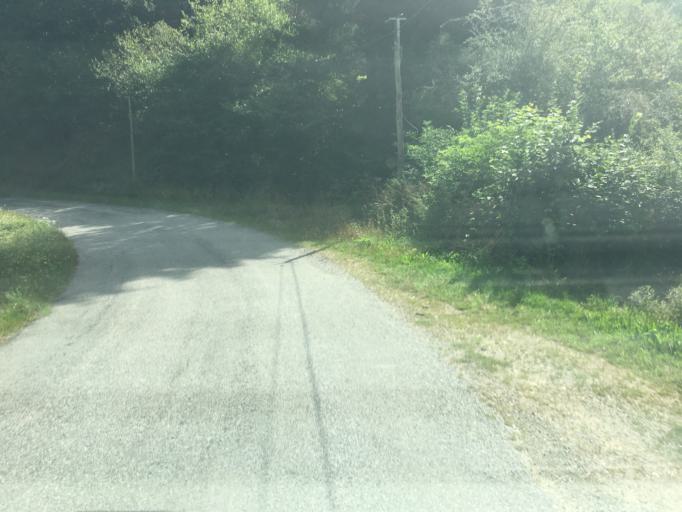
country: FR
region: Auvergne
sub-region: Departement du Cantal
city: Champagnac
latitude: 45.4230
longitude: 2.4074
